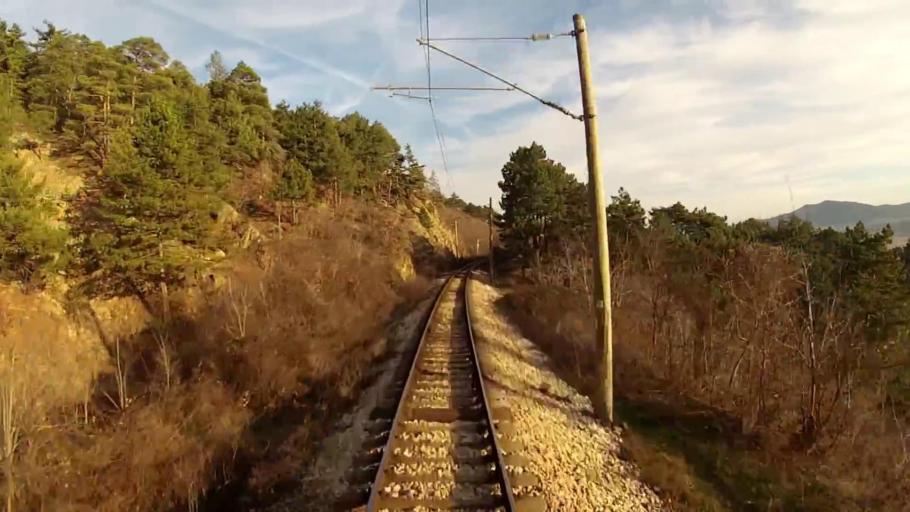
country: BG
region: Plovdiv
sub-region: Obshtina Karlovo
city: Klisura
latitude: 42.7196
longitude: 24.5971
